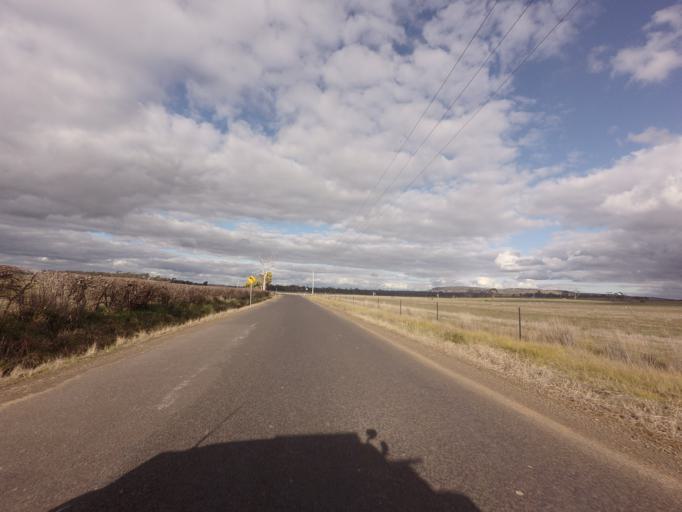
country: AU
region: Tasmania
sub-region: Northern Midlands
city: Longford
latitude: -41.8610
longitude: 147.2495
